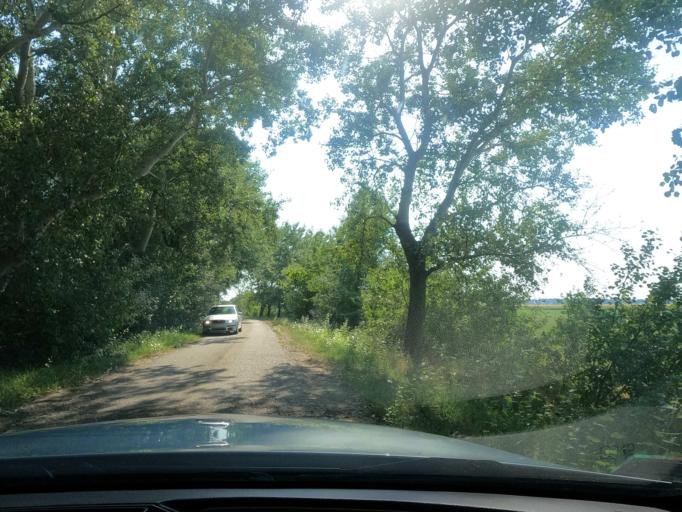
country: RS
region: Autonomna Pokrajina Vojvodina
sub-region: Juznobacki Okrug
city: Becej
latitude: 45.6585
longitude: 19.9025
